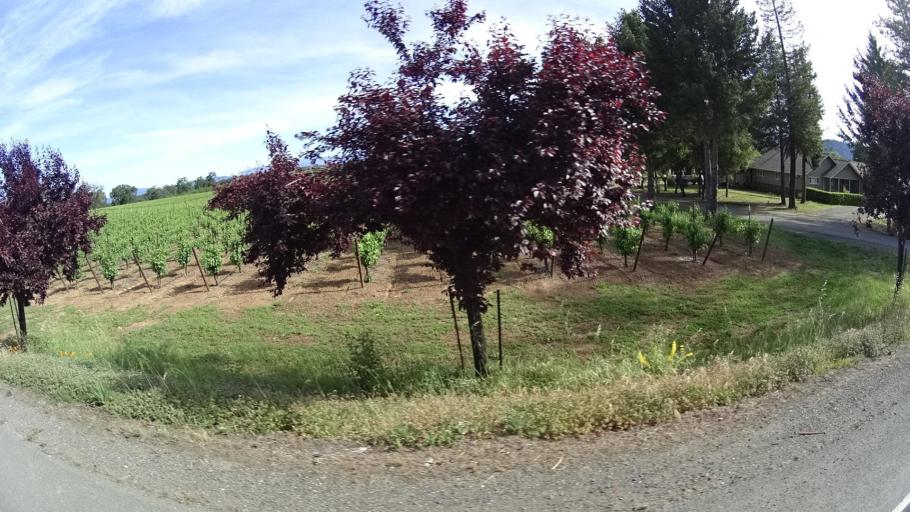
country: US
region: California
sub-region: Lake County
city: Kelseyville
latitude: 38.9823
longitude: -122.8512
